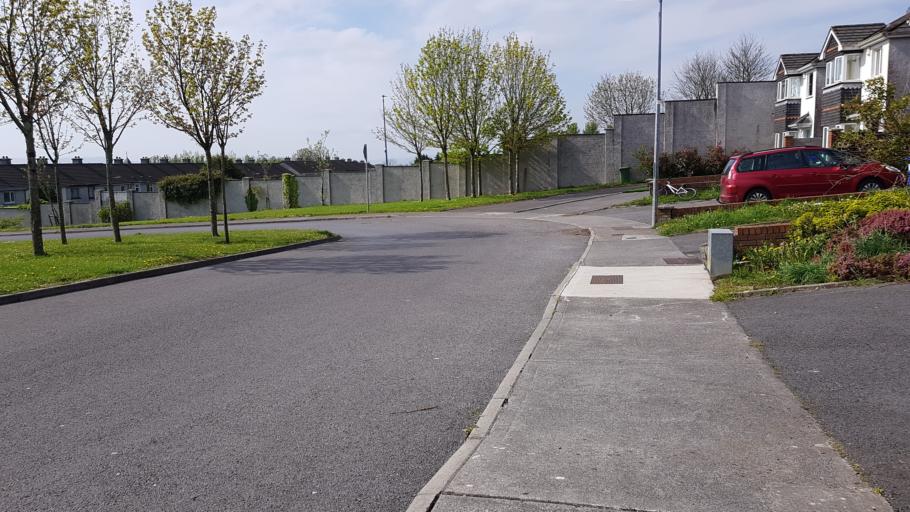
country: IE
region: Connaught
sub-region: County Galway
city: Gaillimh
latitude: 53.2940
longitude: -9.0401
